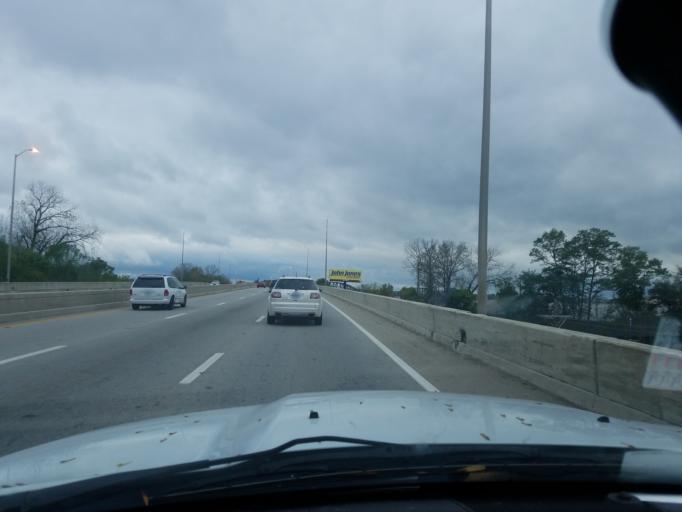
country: US
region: Indiana
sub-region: Floyd County
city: New Albany
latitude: 38.2751
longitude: -85.7898
